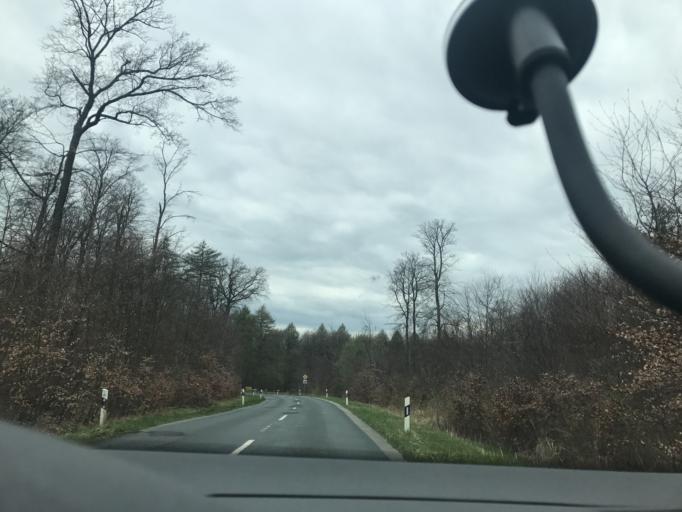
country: DE
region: Lower Saxony
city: Rabke
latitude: 52.1677
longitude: 10.8606
